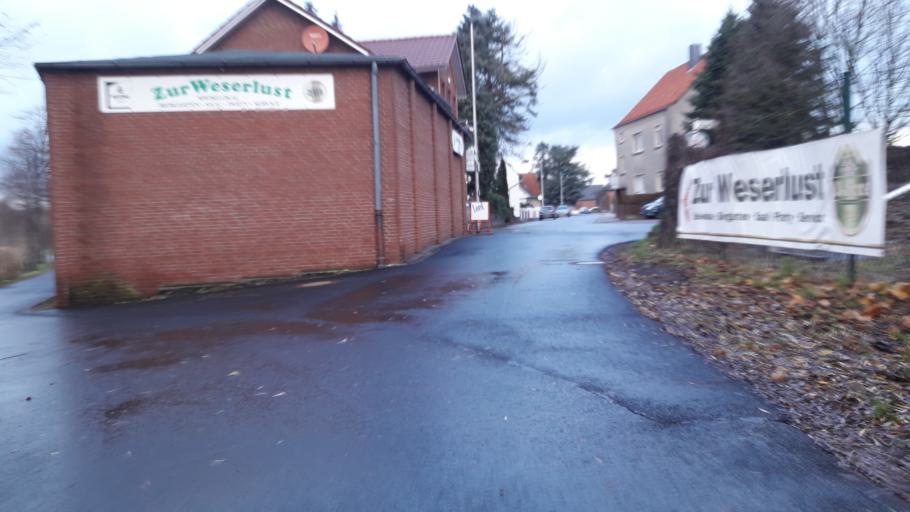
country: DE
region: North Rhine-Westphalia
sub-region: Regierungsbezirk Detmold
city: Minden
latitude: 52.3063
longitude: 8.9305
